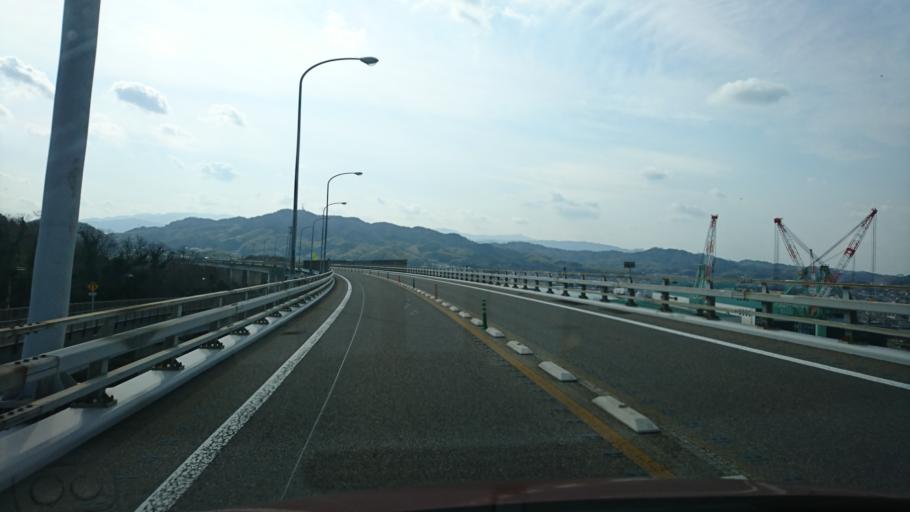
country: JP
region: Hiroshima
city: Takehara
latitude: 34.1108
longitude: 132.9767
